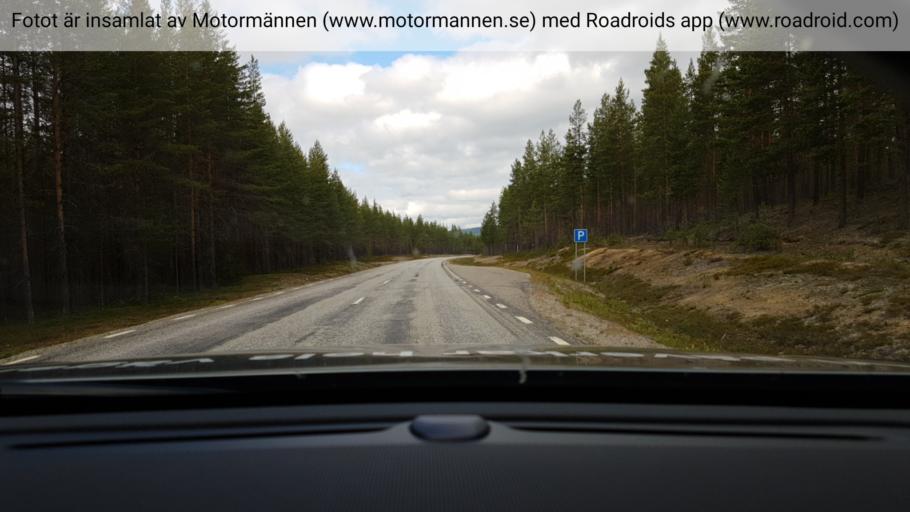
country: SE
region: Vaesterbotten
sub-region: Mala Kommun
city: Mala
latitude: 64.9190
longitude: 18.6306
